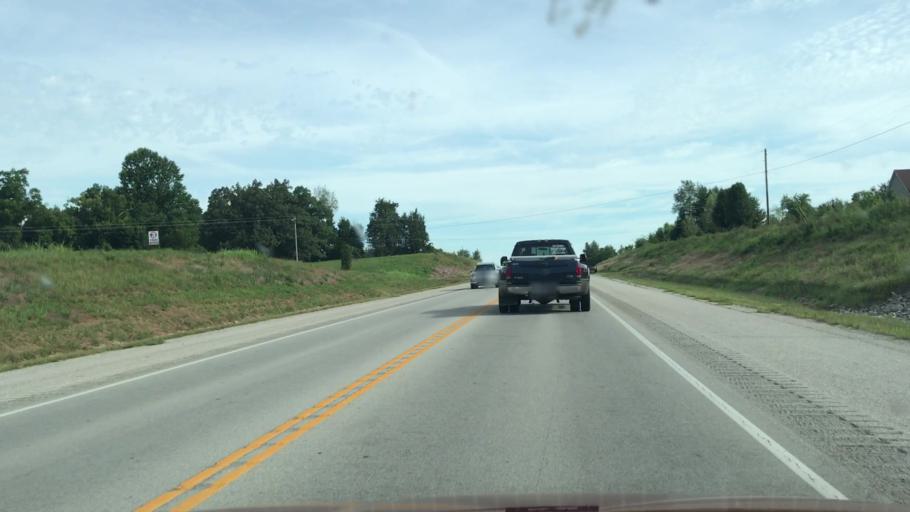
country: US
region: Kentucky
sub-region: Edmonson County
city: Brownsville
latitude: 37.1512
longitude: -86.2211
